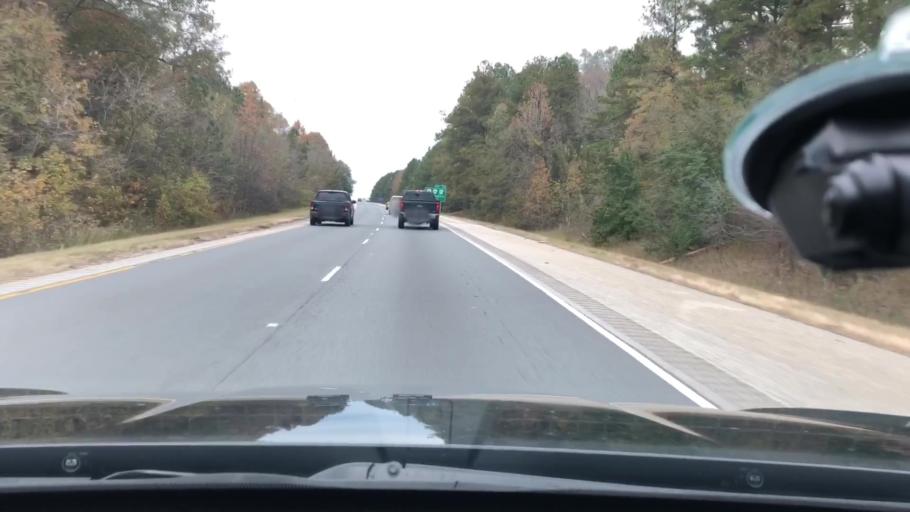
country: US
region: Arkansas
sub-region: Clark County
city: Arkadelphia
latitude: 34.1000
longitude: -93.1028
